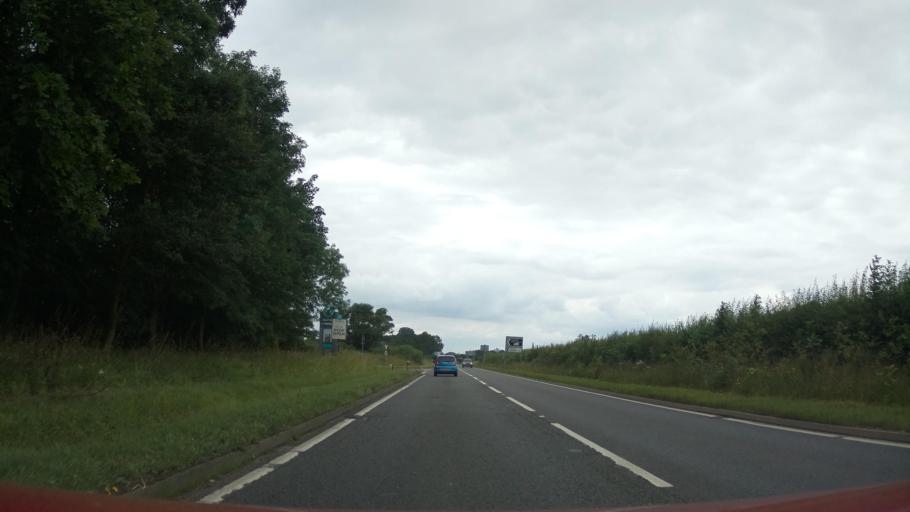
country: GB
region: England
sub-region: Lincolnshire
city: Long Bennington
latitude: 52.9356
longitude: -0.7630
